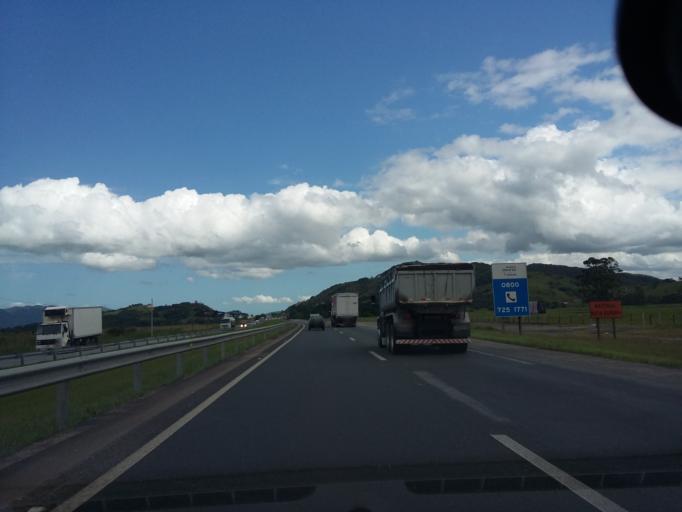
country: BR
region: Santa Catarina
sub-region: Tijucas
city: Tijucas
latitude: -27.2638
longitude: -48.6318
